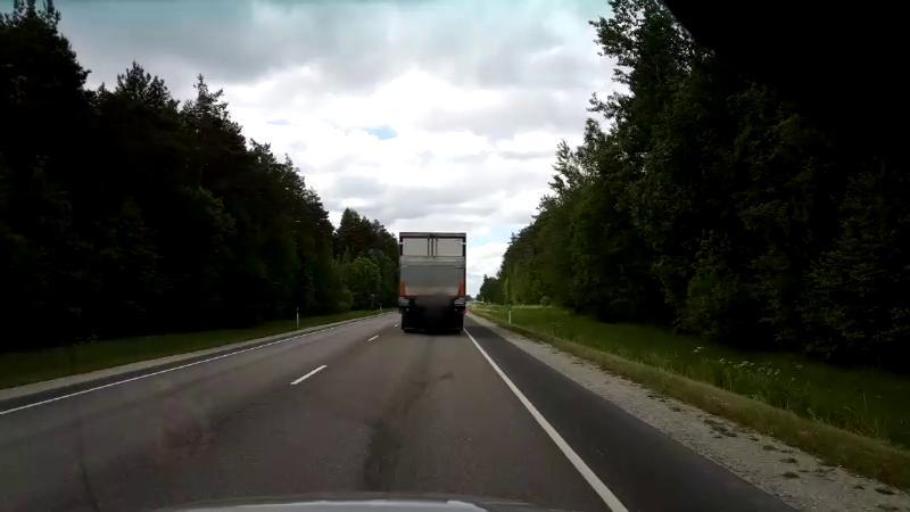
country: EE
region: Raplamaa
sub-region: Maerjamaa vald
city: Marjamaa
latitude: 58.7538
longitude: 24.4233
